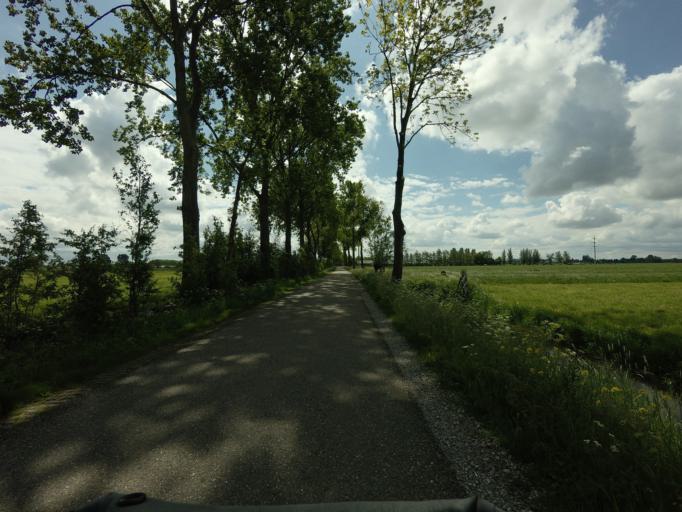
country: NL
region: South Holland
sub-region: Gemeente Gorinchem
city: Gorinchem
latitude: 51.8563
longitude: 4.9407
